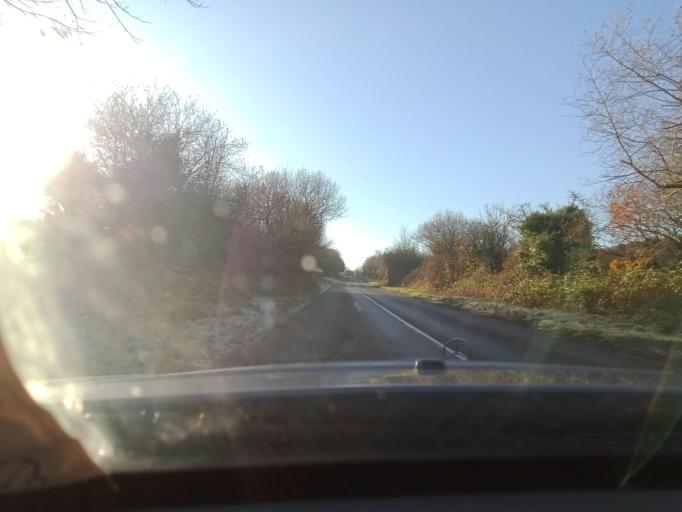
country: IE
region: Leinster
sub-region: Kilkenny
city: Graiguenamanagh
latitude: 52.5819
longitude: -6.9487
